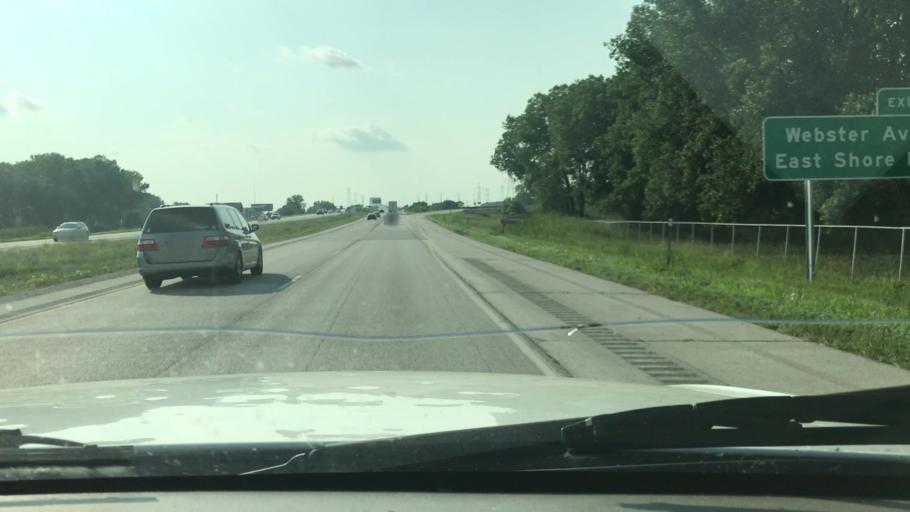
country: US
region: Wisconsin
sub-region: Brown County
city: Green Bay
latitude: 44.5243
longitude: -87.9790
